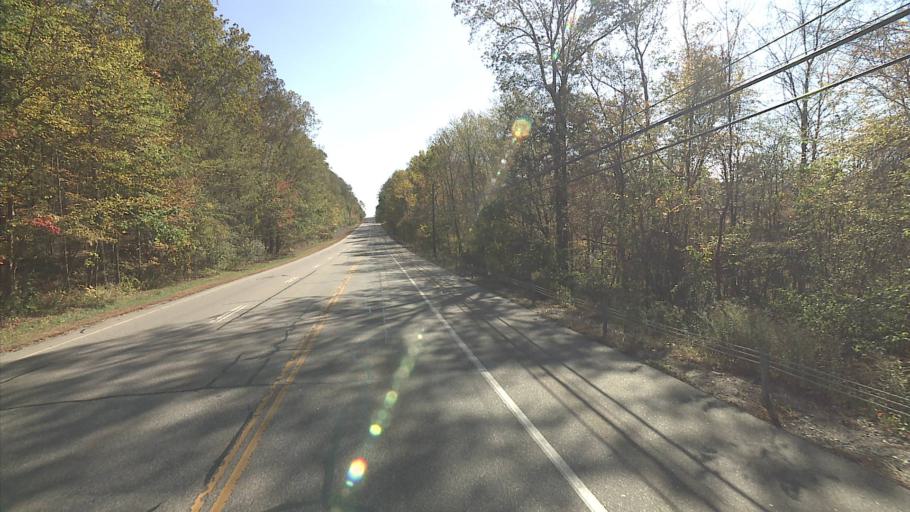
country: US
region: Connecticut
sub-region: Windham County
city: Windham
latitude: 41.7731
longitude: -72.0673
